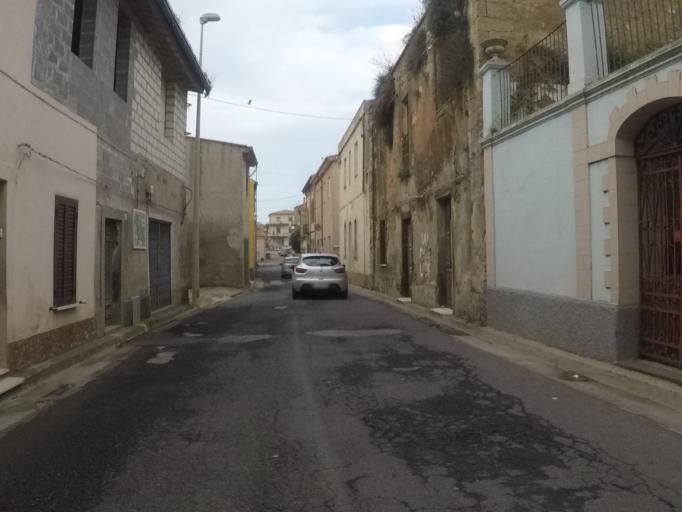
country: IT
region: Sardinia
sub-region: Provincia di Oristano
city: Tresnuraghes
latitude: 40.2521
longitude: 8.5208
